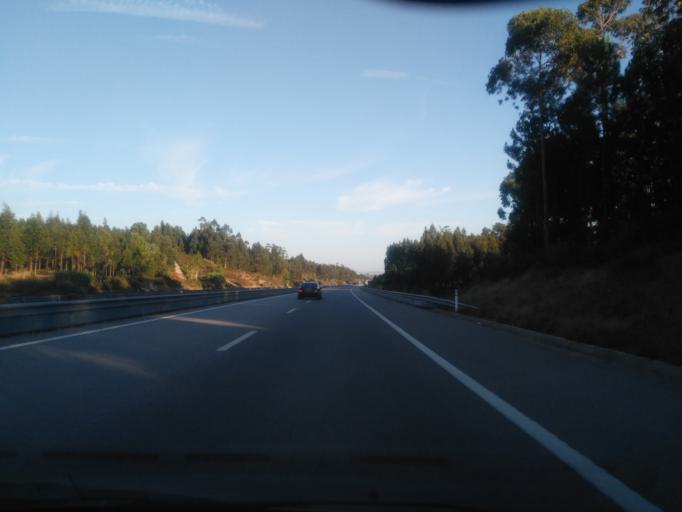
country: PT
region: Coimbra
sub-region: Figueira da Foz
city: Alhadas
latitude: 40.1688
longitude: -8.7873
